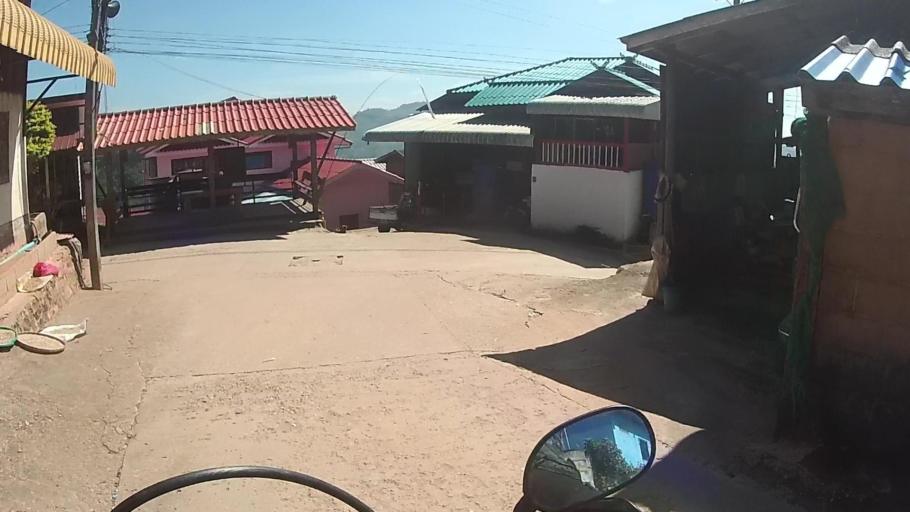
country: TH
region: Chiang Mai
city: Phrao
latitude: 19.3912
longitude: 99.3377
